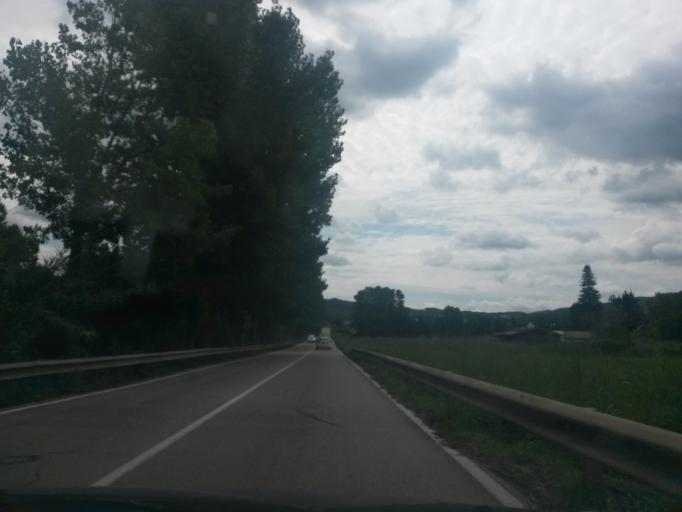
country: ES
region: Catalonia
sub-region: Provincia de Girona
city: la Cellera de Ter
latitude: 41.9661
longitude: 2.6263
